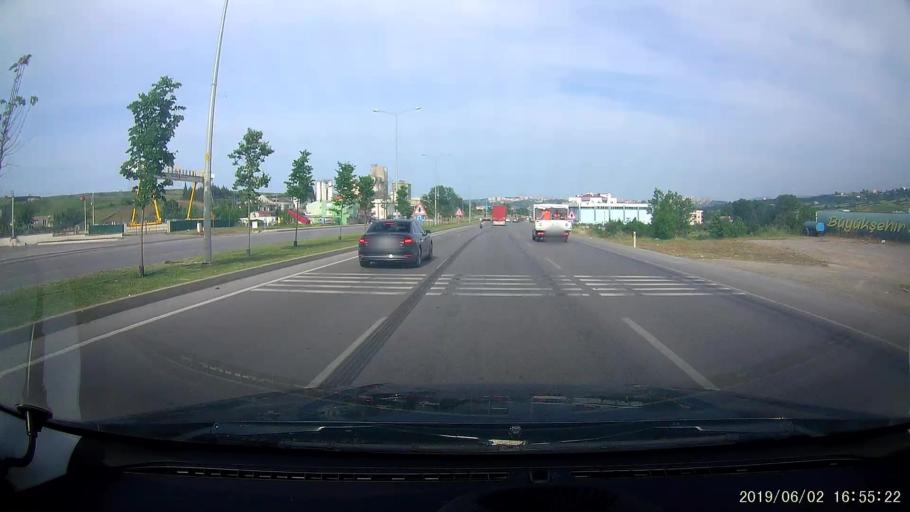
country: TR
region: Samsun
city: Samsun
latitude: 41.2929
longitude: 36.2530
